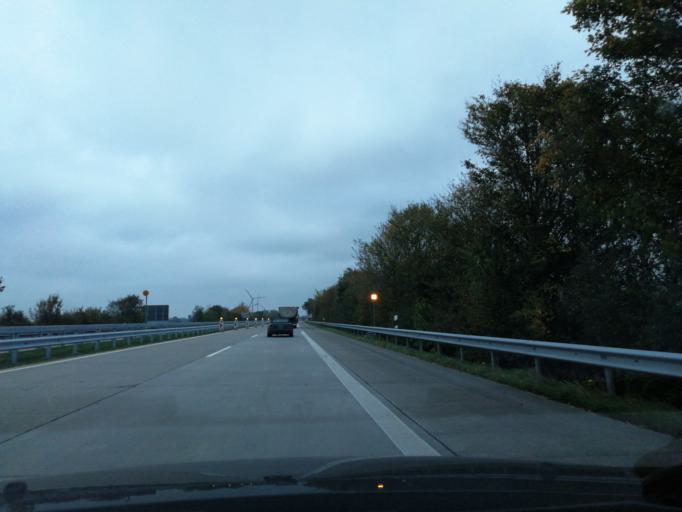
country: DE
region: Lower Saxony
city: Sande
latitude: 53.5352
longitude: 8.0220
